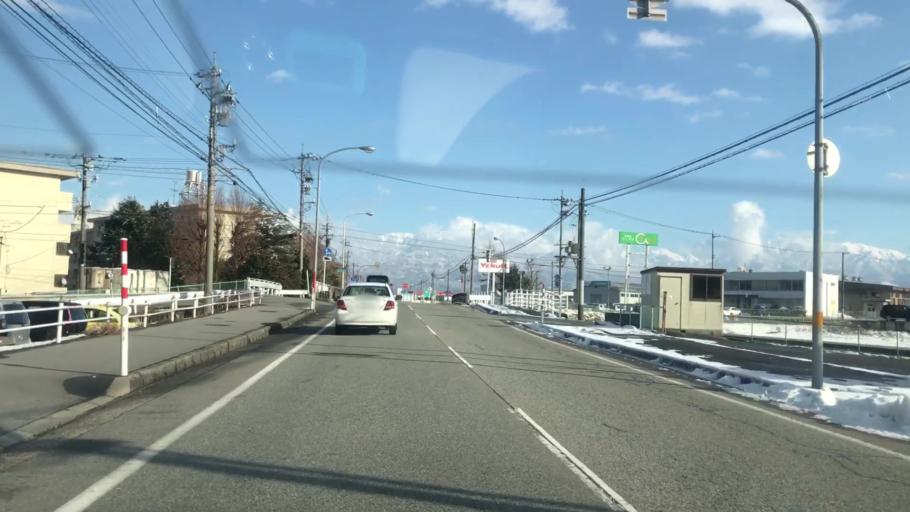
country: JP
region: Toyama
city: Toyama-shi
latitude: 36.6732
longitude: 137.2667
